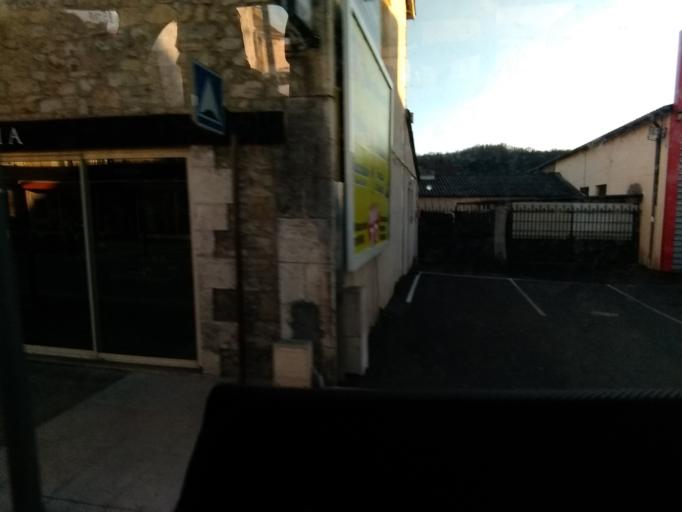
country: FR
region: Aquitaine
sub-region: Departement de la Dordogne
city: Terrasson-Lavilledieu
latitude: 45.1301
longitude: 1.2985
